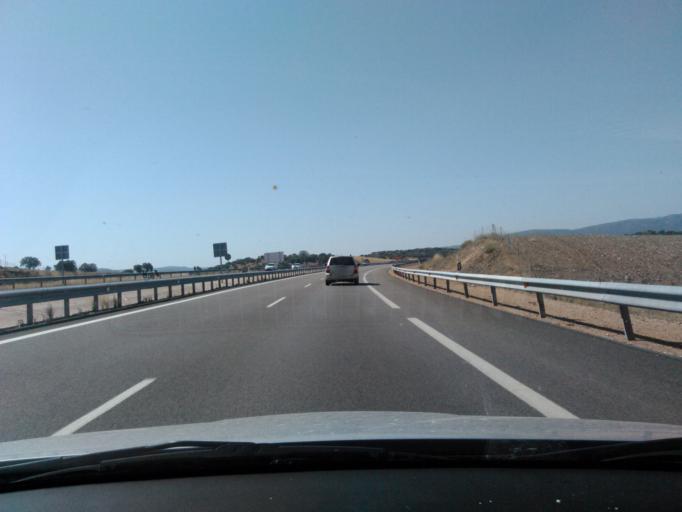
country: ES
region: Castille-La Mancha
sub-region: Provincia de Ciudad Real
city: Viso del Marques
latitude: 38.4874
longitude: -3.5016
